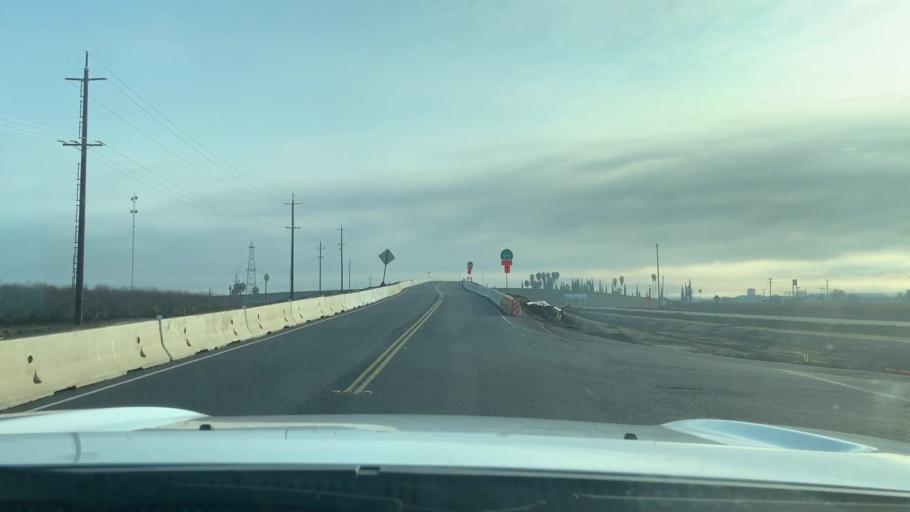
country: US
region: California
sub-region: Kern County
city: McFarland
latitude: 35.6020
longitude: -119.2164
